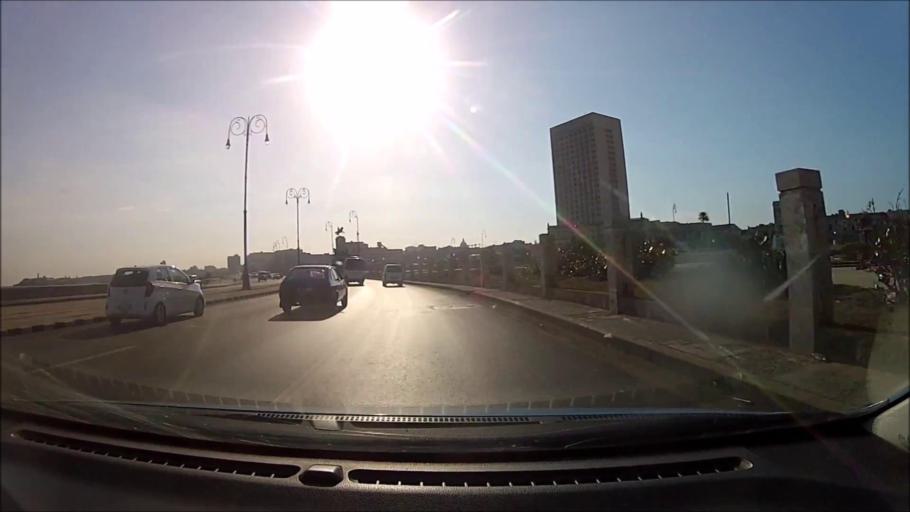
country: CU
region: La Habana
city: Centro Habana
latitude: 23.1416
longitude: -82.3740
